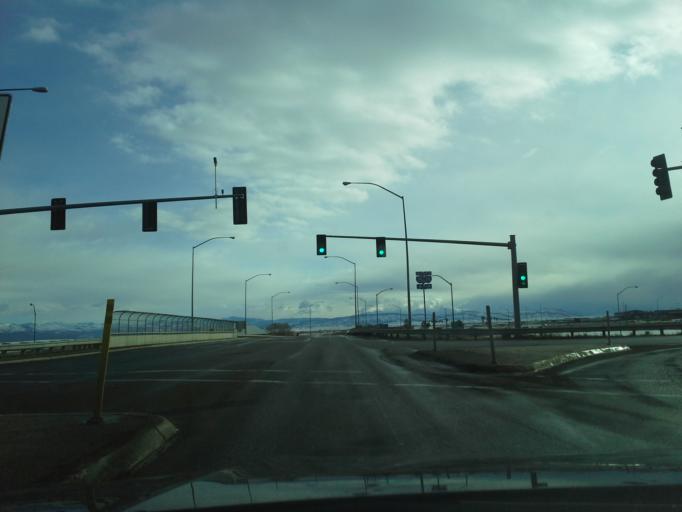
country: US
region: Montana
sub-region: Lewis and Clark County
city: Helena
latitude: 46.6068
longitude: -112.0093
